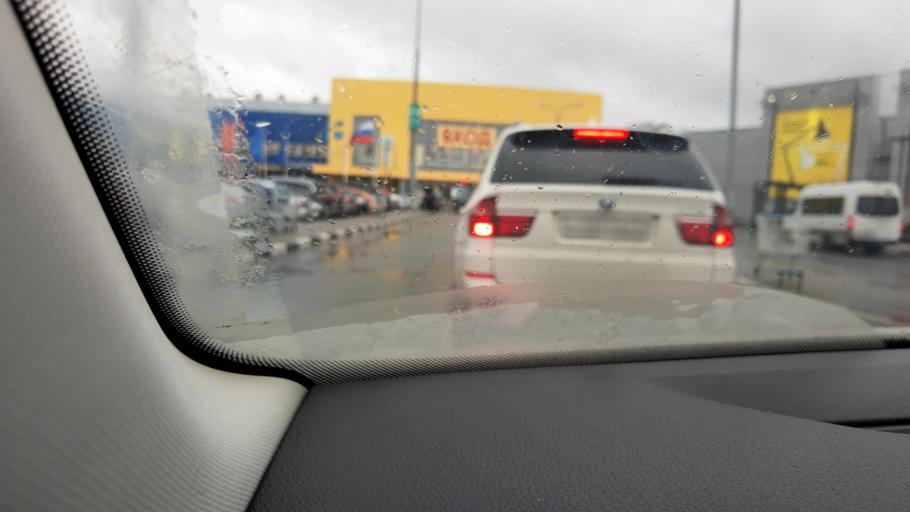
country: RU
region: Moscow
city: Tyoply Stan
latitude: 55.6044
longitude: 37.4932
